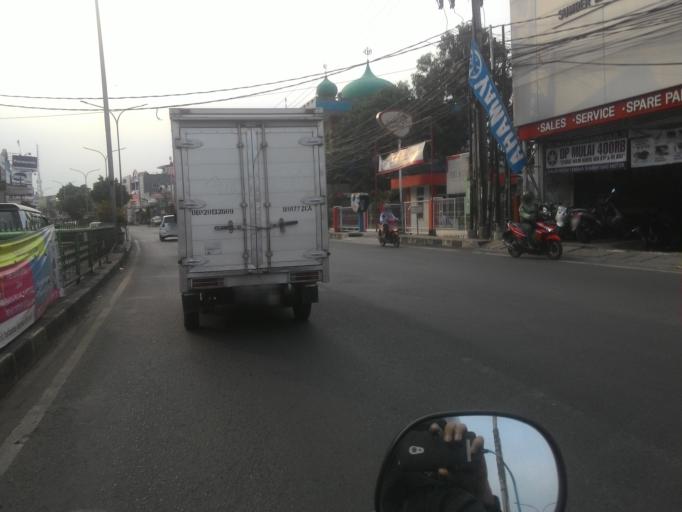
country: ID
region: West Java
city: Depok
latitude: -6.3890
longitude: 106.8192
